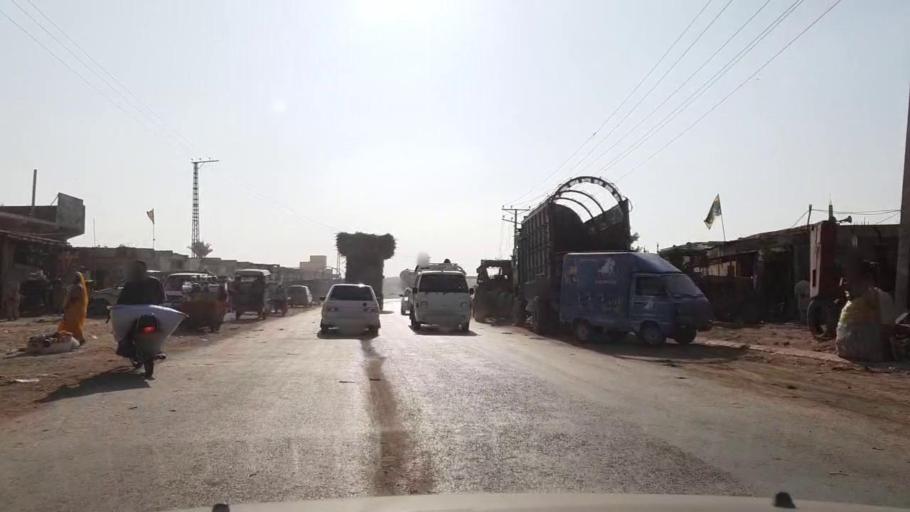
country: PK
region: Sindh
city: Tando Muhammad Khan
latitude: 25.1160
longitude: 68.5348
